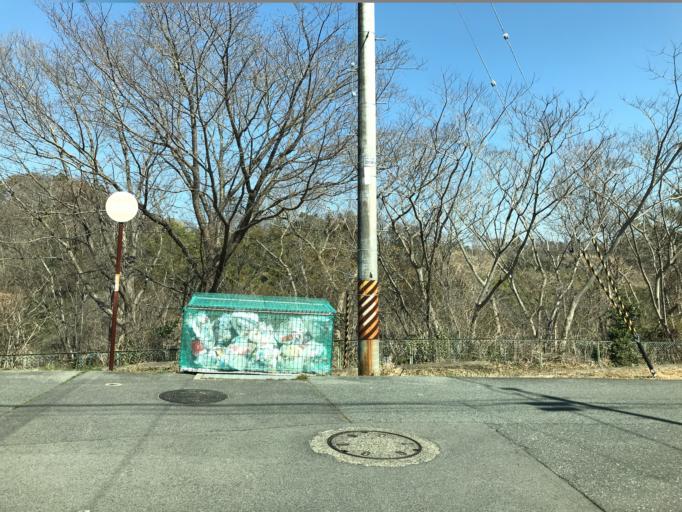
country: JP
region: Fukushima
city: Iwaki
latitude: 37.0487
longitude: 140.8525
